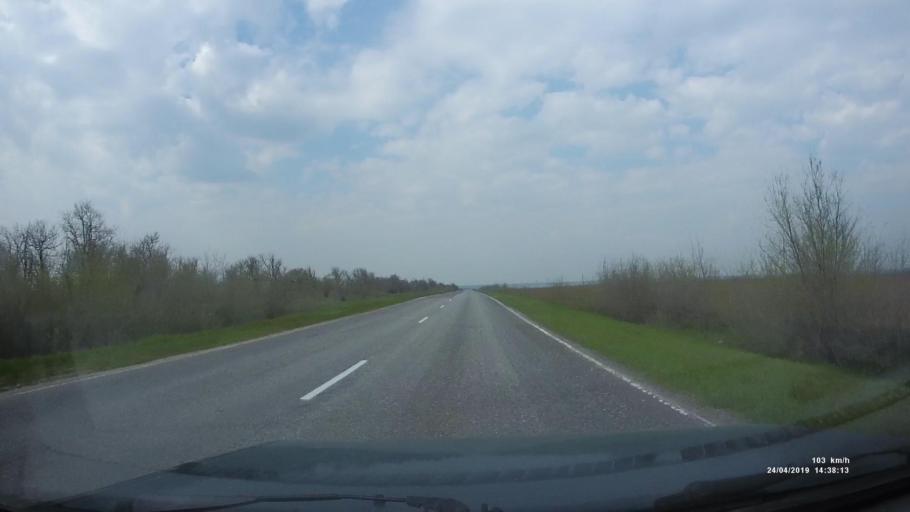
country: RU
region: Rostov
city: Remontnoye
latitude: 46.3982
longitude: 43.8861
